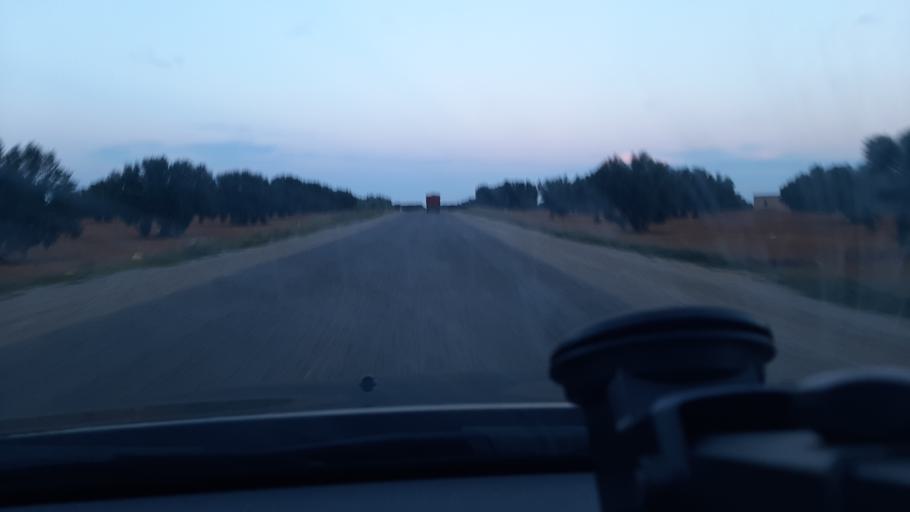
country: TN
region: Al Mahdiyah
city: Shurban
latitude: 35.0048
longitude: 10.4189
